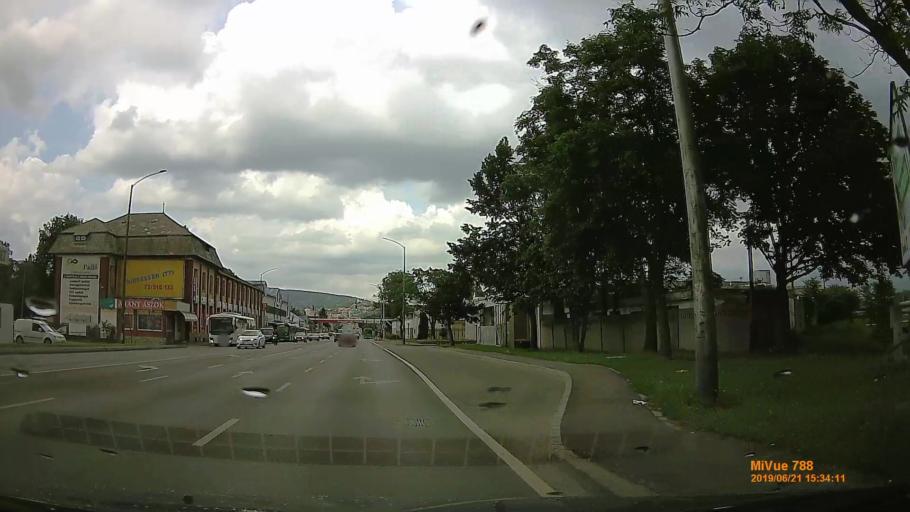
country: HU
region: Baranya
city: Pecs
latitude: 46.0615
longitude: 18.2306
